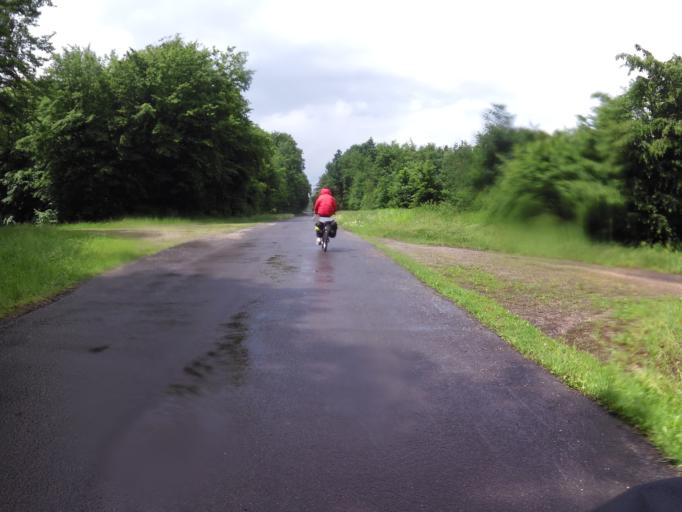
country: FR
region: Champagne-Ardenne
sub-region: Departement de la Marne
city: Sermaize-les-Bains
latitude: 48.7457
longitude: 4.9760
